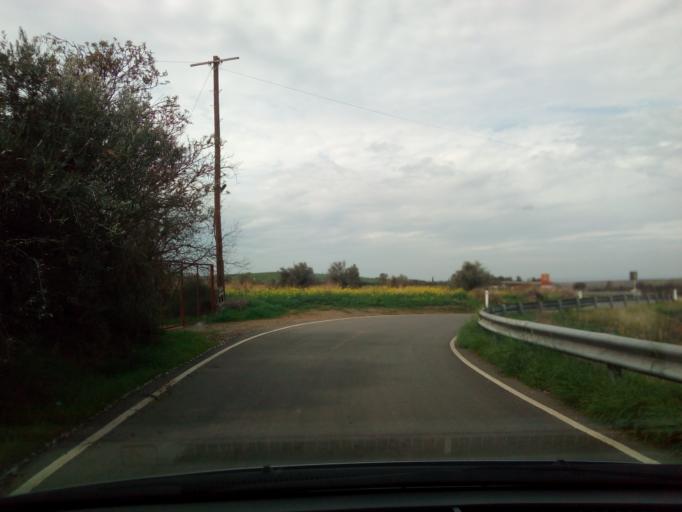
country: CY
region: Lefkosia
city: Astromeritis
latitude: 35.0984
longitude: 32.9843
